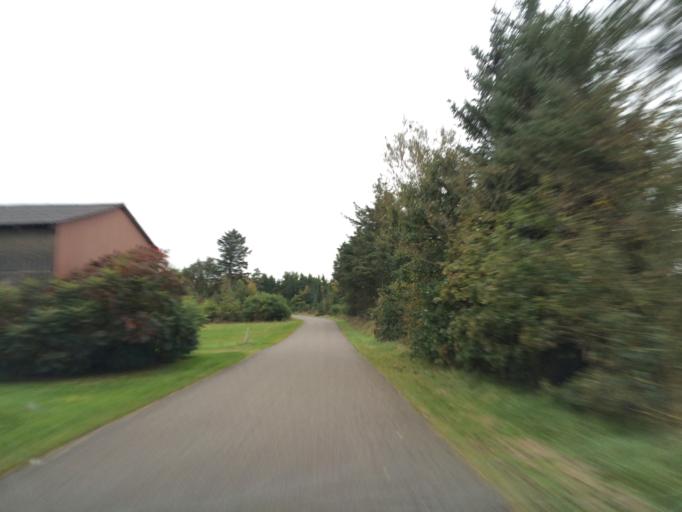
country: DK
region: Central Jutland
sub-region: Holstebro Kommune
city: Ulfborg
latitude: 56.2295
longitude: 8.4365
